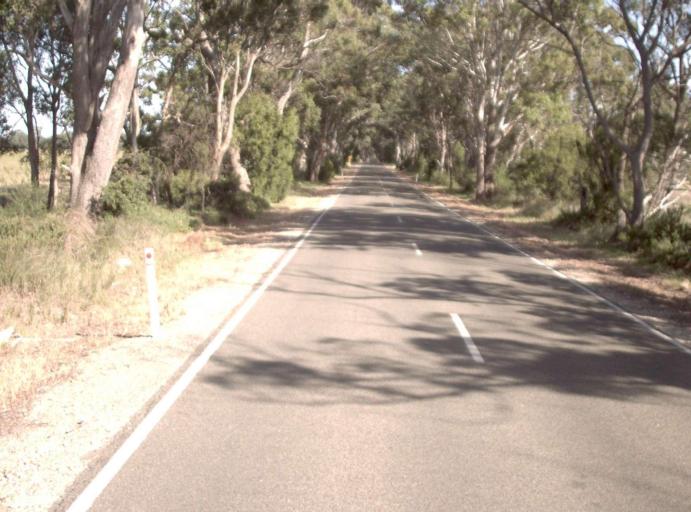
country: AU
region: Victoria
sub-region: East Gippsland
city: Lakes Entrance
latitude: -37.8089
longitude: 147.8434
